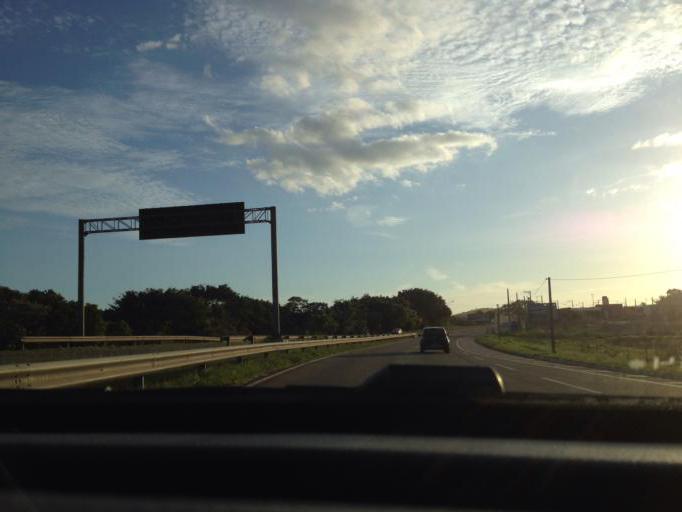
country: BR
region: Espirito Santo
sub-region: Guarapari
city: Guarapari
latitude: -20.6231
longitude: -40.4342
